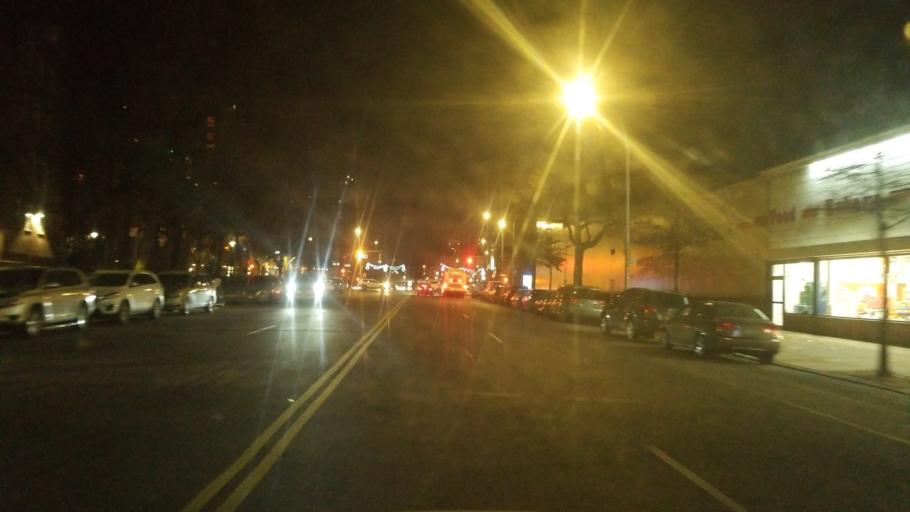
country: US
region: New York
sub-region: New York County
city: Manhattan
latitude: 40.8126
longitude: -73.9261
